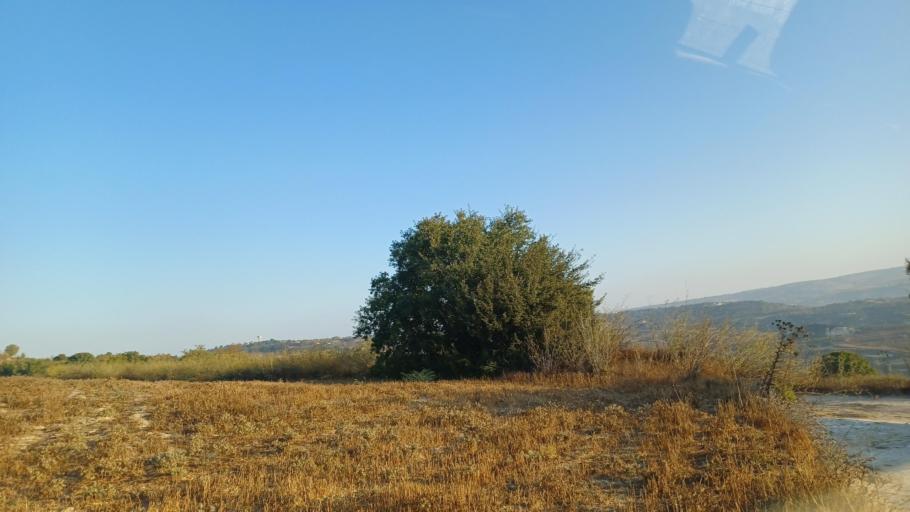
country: CY
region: Pafos
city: Mesogi
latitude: 34.8641
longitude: 32.5114
